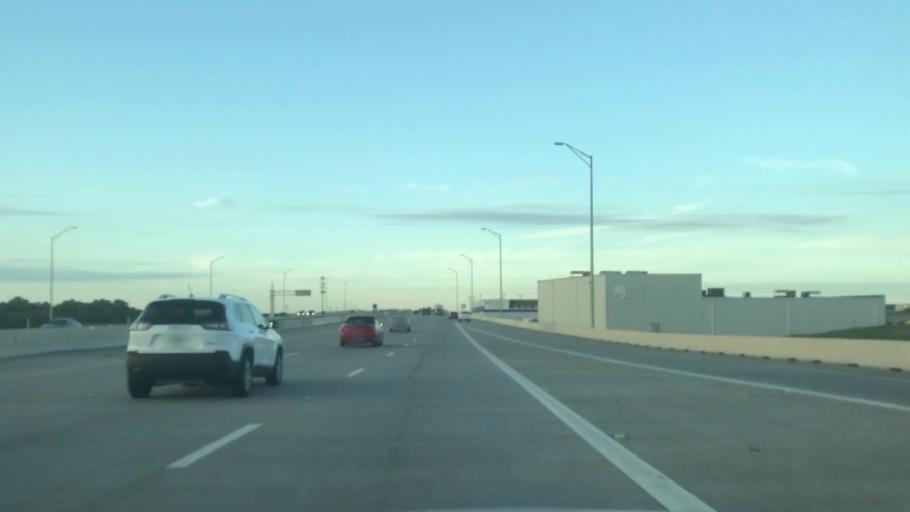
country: US
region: Texas
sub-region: Dallas County
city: Farmers Branch
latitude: 32.9204
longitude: -96.9328
